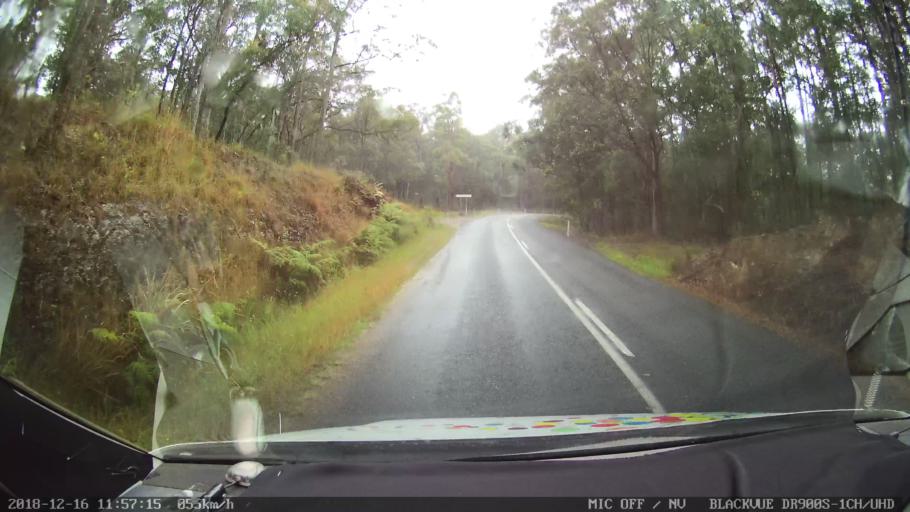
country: AU
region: New South Wales
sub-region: Tenterfield Municipality
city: Carrolls Creek
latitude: -28.9162
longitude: 152.3057
